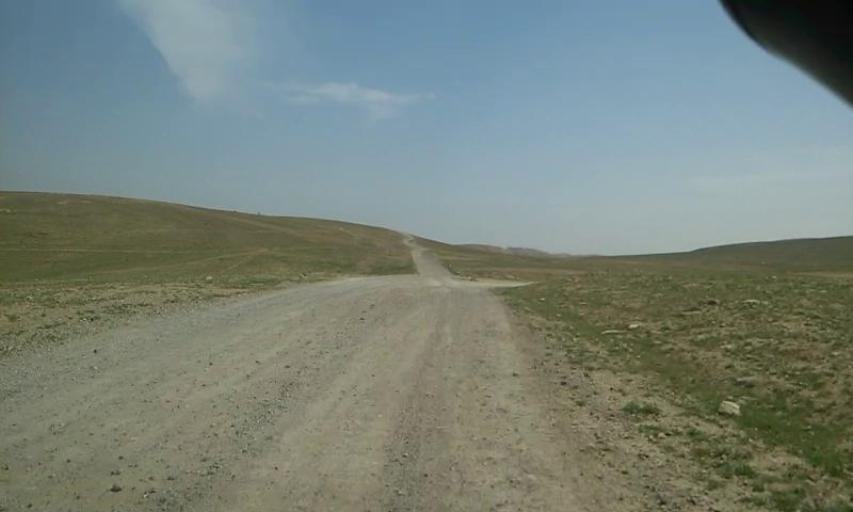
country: PS
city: `Arab ar Rashaydah
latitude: 31.5252
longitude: 35.2960
